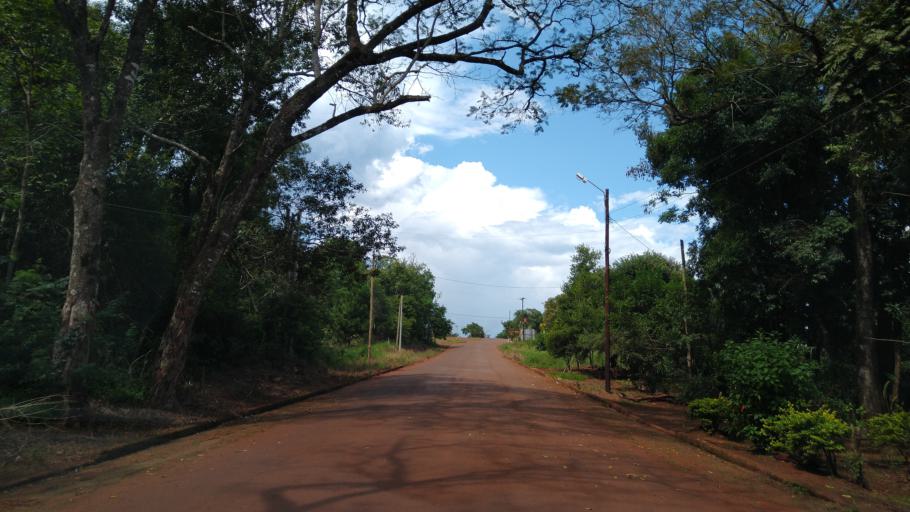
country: AR
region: Misiones
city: Puerto Libertad
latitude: -25.9664
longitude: -54.5951
